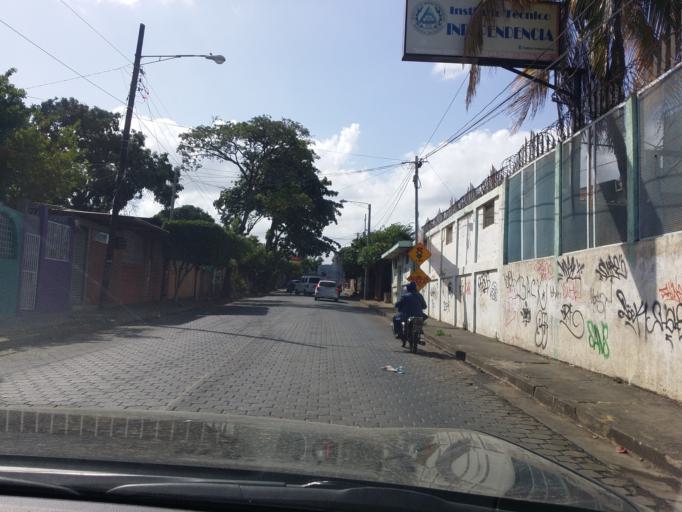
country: NI
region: Managua
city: Managua
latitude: 12.1272
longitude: -86.2343
